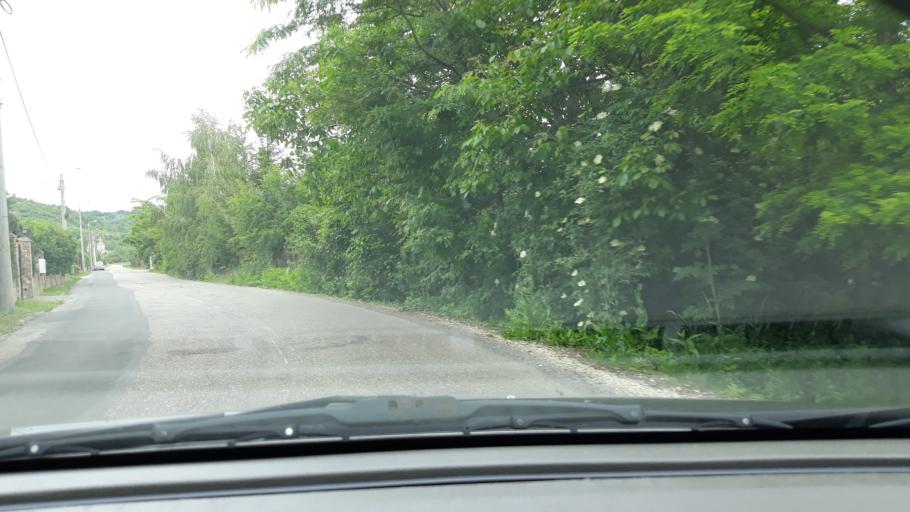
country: RO
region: Bihor
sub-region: Comuna Osorheiu
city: Alparea
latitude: 47.0532
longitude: 22.0006
